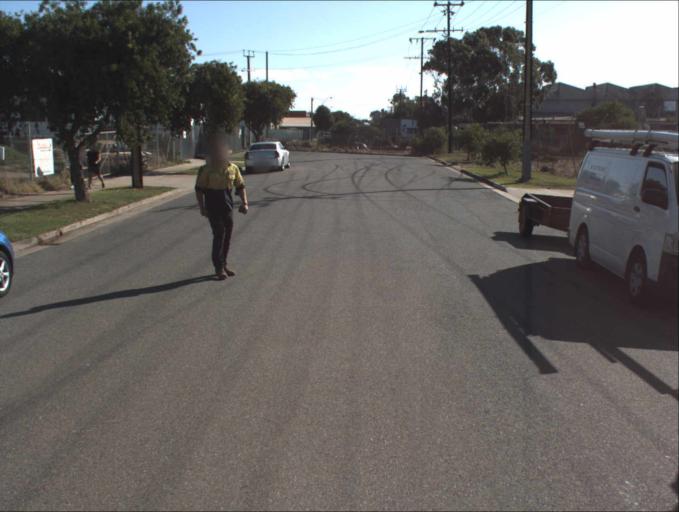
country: AU
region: South Australia
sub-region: Port Adelaide Enfield
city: Alberton
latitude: -34.8464
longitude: 138.5282
